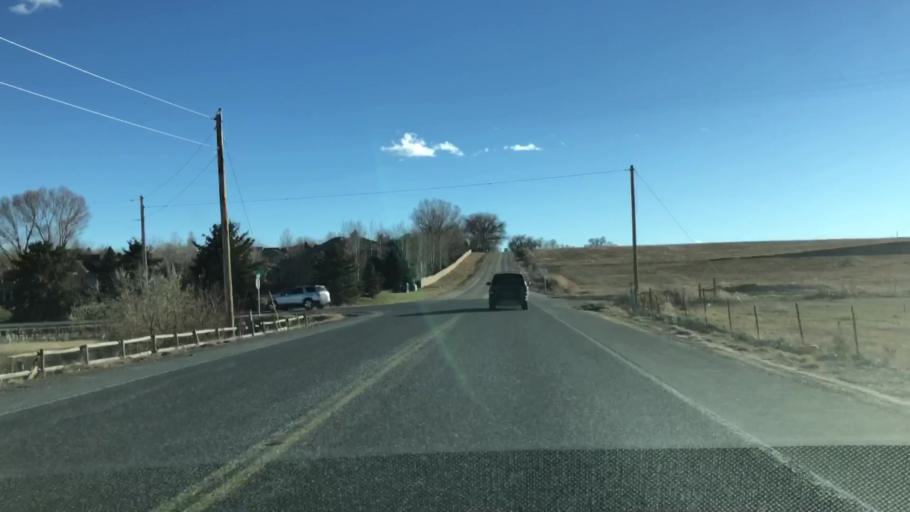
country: US
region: Colorado
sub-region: Weld County
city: Windsor
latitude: 40.4872
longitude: -104.9820
